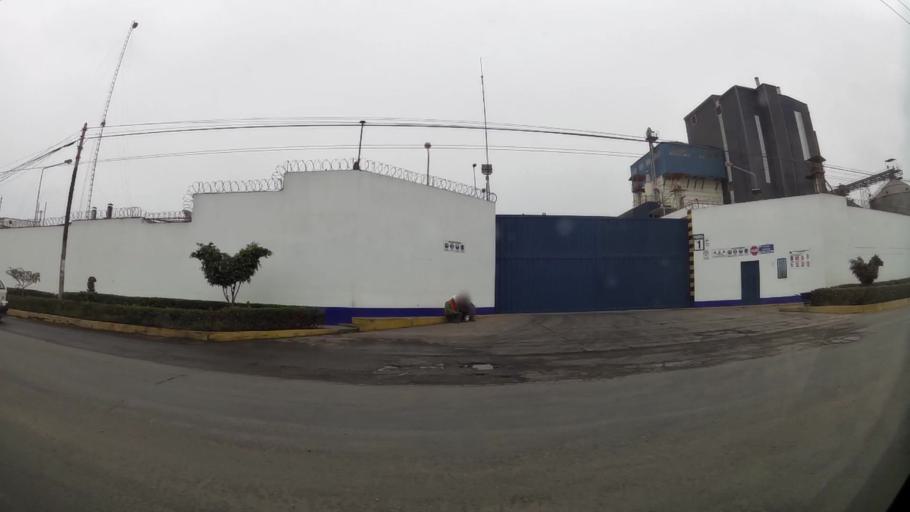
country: PE
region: Lima
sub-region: Lima
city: Punta Hermosa
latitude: -12.2975
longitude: -76.8405
